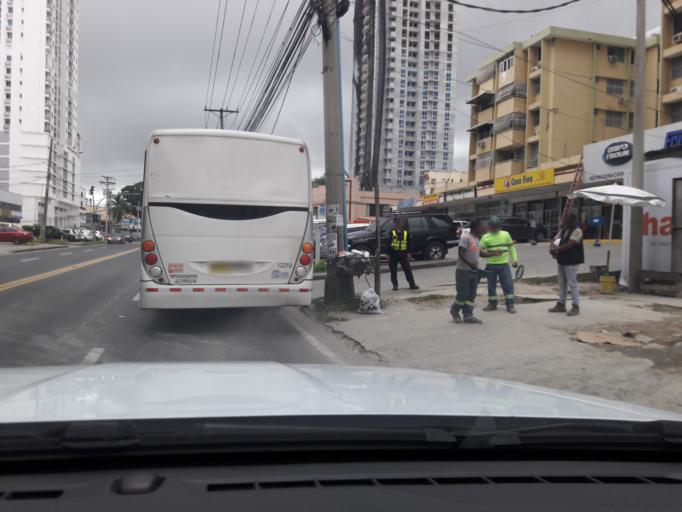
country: PA
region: Panama
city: Panama
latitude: 9.0072
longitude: -79.5088
